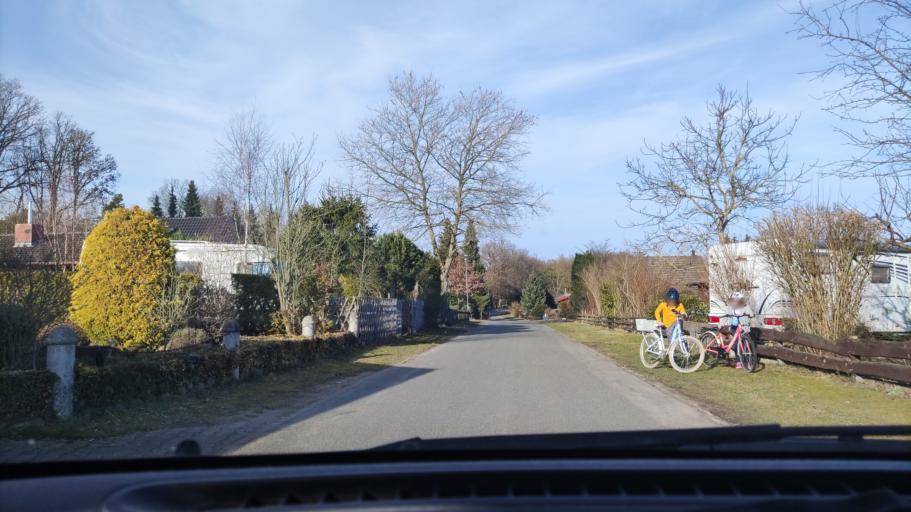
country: DE
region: Lower Saxony
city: Tosterglope
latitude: 53.1968
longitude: 10.8562
